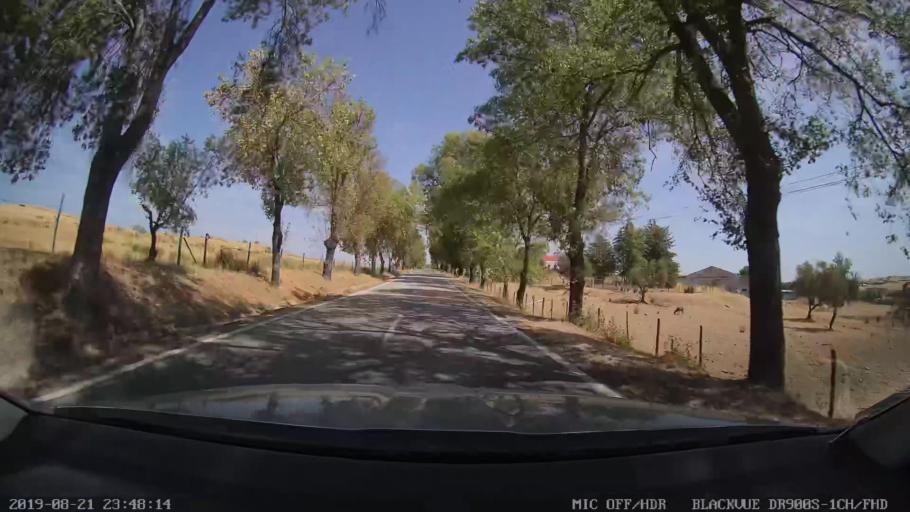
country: PT
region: Castelo Branco
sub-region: Idanha-A-Nova
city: Idanha-a-Nova
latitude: 39.8622
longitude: -7.2582
